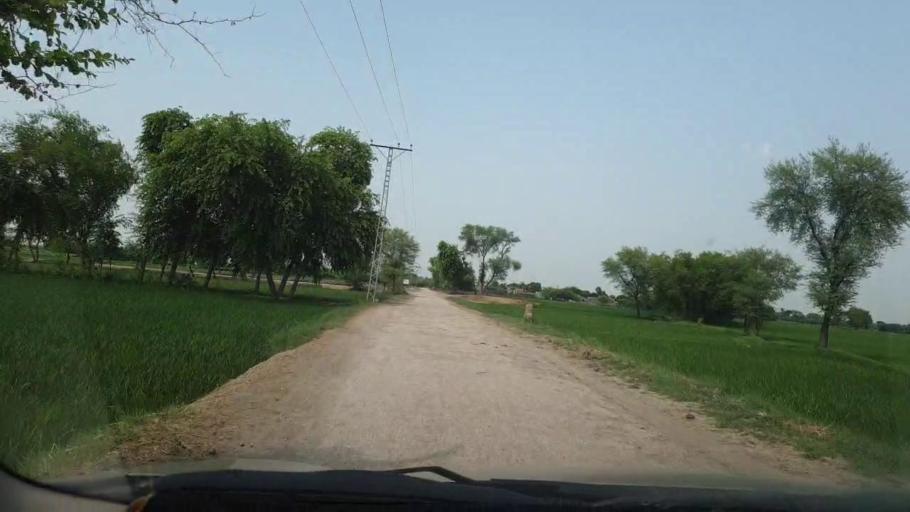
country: PK
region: Sindh
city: Larkana
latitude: 27.5830
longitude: 68.1439
